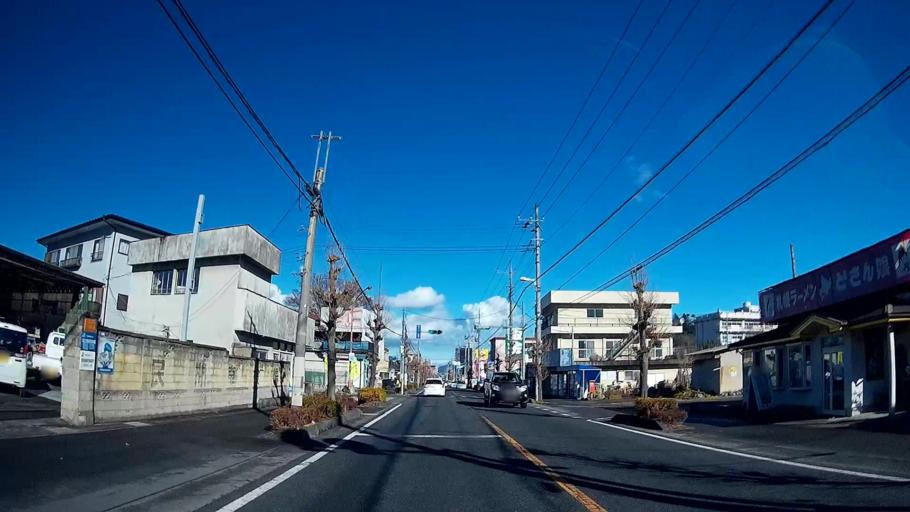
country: JP
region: Saitama
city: Chichibu
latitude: 36.0103
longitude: 139.0921
